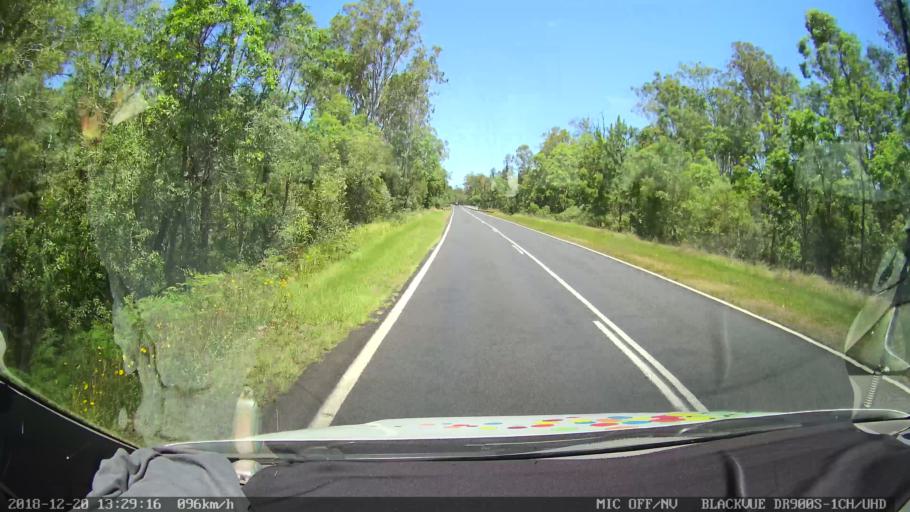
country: AU
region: New South Wales
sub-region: Clarence Valley
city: Gordon
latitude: -29.1867
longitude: 152.9889
